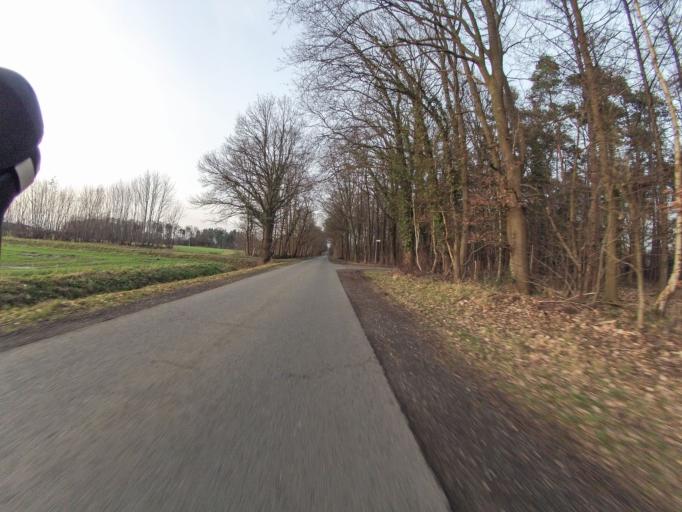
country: DE
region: North Rhine-Westphalia
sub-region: Regierungsbezirk Munster
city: Steinfurt
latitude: 52.1790
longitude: 7.3318
